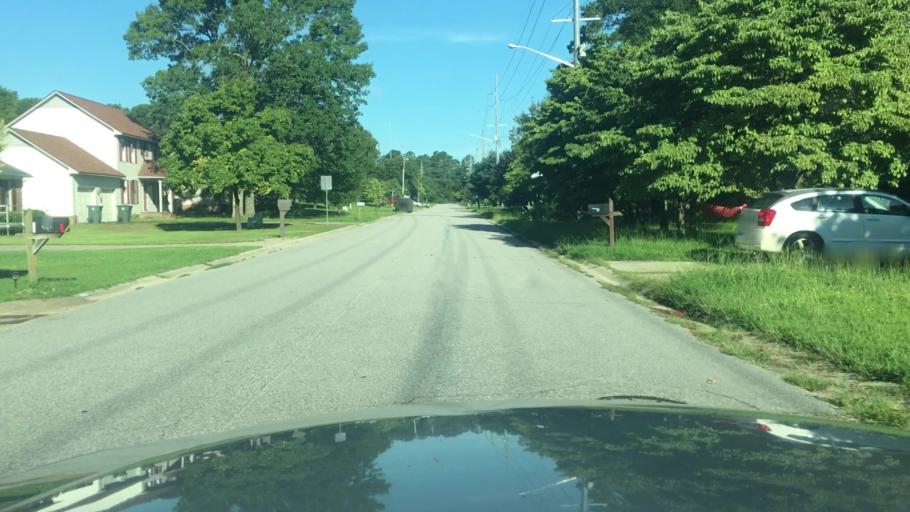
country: US
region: North Carolina
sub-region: Cumberland County
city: Fayetteville
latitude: 35.1306
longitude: -78.8884
